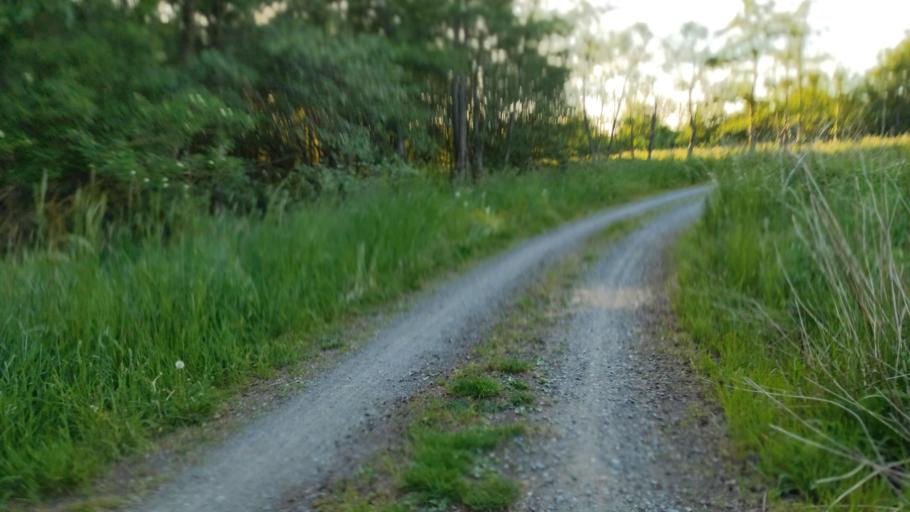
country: DE
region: Lower Saxony
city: Sickte
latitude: 52.2227
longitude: 10.5958
